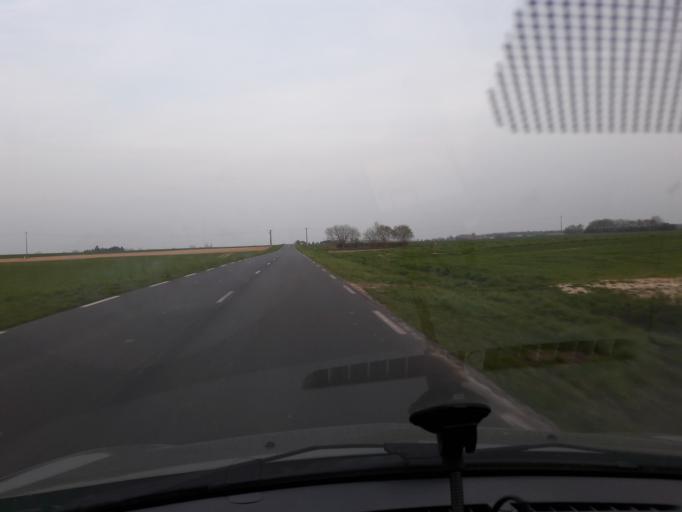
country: FR
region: Nord-Pas-de-Calais
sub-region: Departement du Nord
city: Recquignies
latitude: 50.2572
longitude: 4.0483
